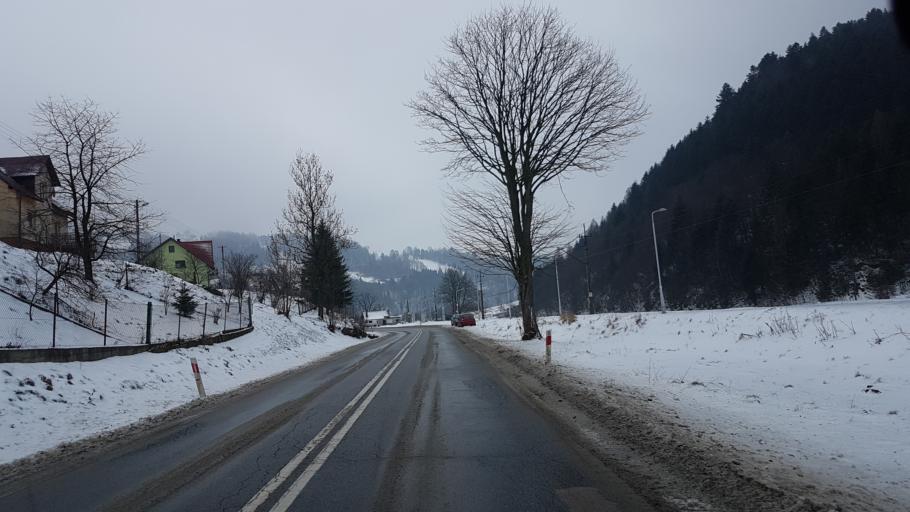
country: PL
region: Lesser Poland Voivodeship
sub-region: Powiat nowosadecki
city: Piwniczna-Zdroj
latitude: 49.3883
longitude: 20.7531
